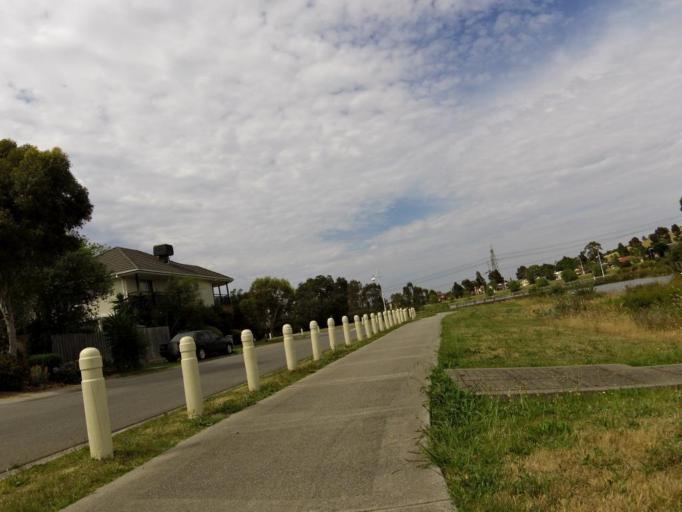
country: AU
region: Victoria
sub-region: Whittlesea
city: Mill Park
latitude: -37.6369
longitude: 145.0696
